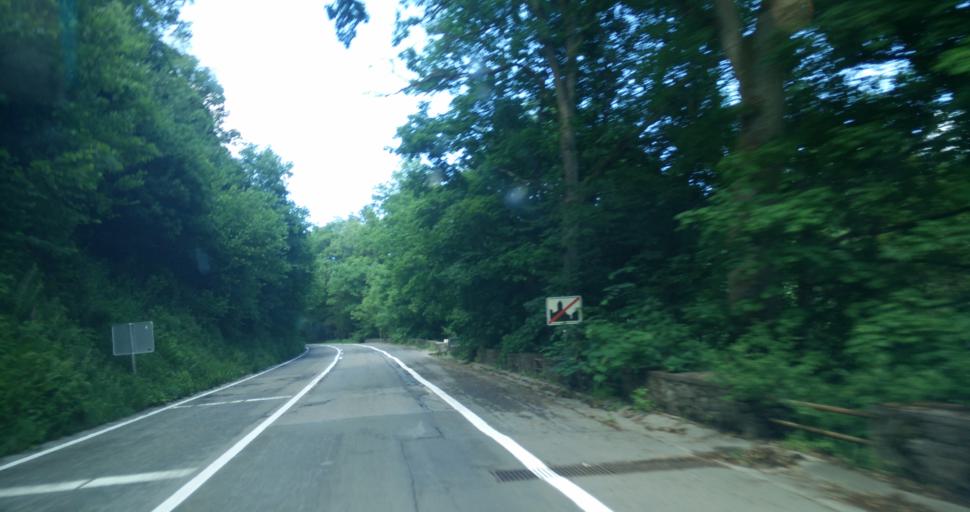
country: BE
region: Wallonia
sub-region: Province du Luxembourg
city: La Roche-en-Ardenne
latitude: 50.1700
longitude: 5.6293
